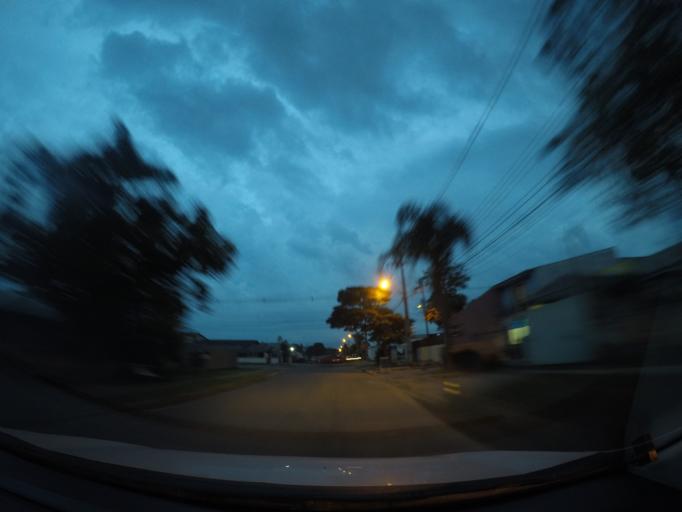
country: BR
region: Parana
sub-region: Sao Jose Dos Pinhais
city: Sao Jose dos Pinhais
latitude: -25.5174
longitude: -49.2243
